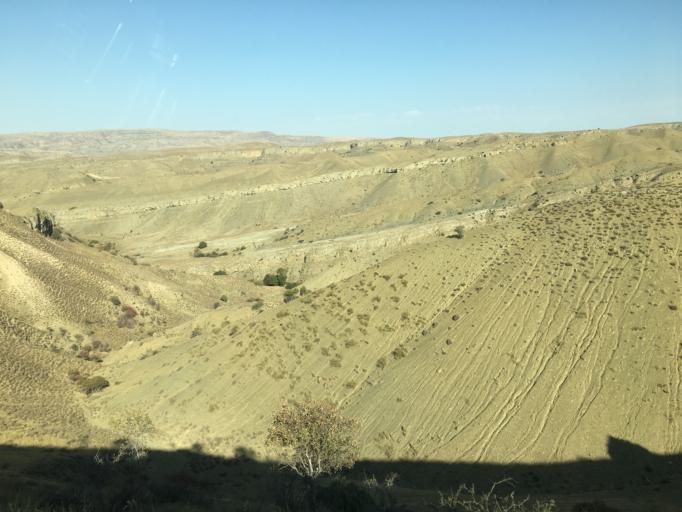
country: TM
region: Balkan
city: Magtymguly
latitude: 38.3014
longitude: 56.7947
